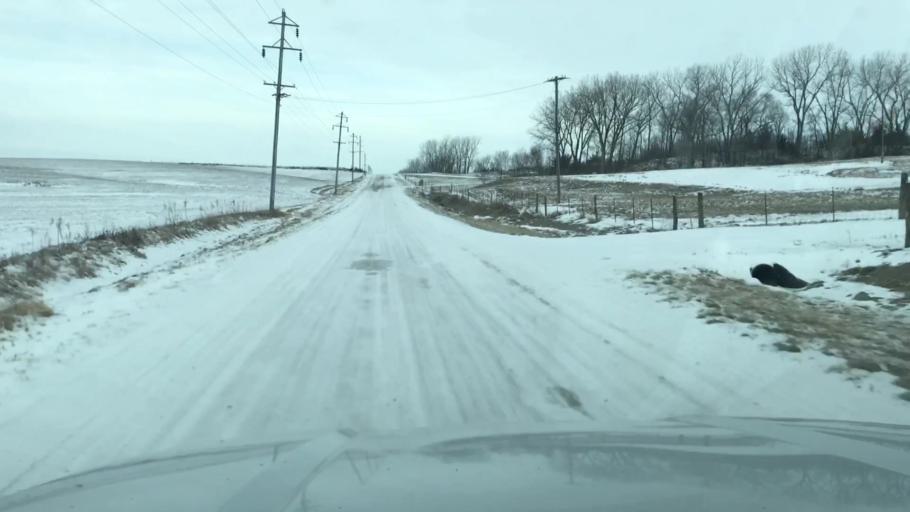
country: US
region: Missouri
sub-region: Holt County
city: Oregon
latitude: 40.1301
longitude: -95.0568
